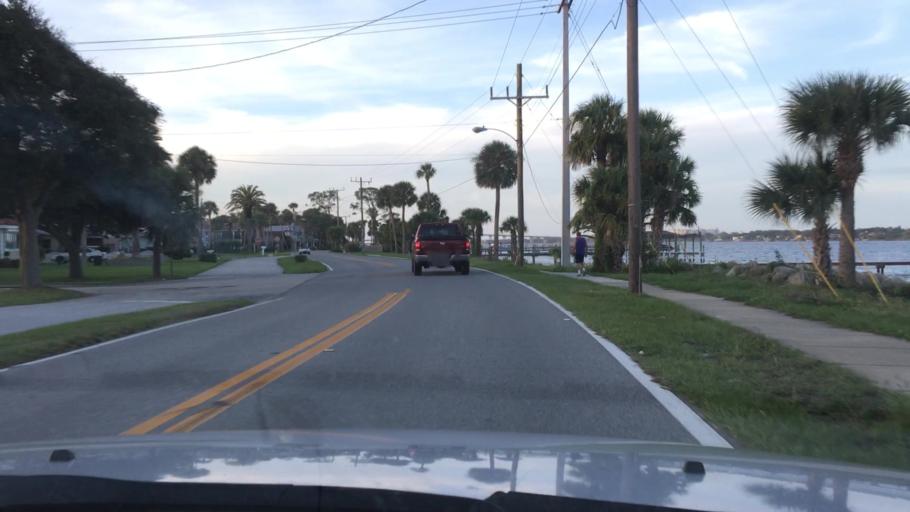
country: US
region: Florida
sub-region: Volusia County
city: Ormond Beach
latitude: 29.2701
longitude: -81.0474
